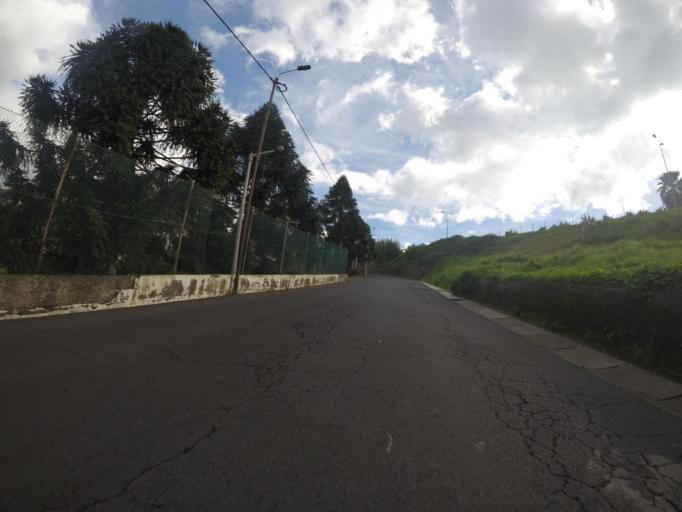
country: PT
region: Madeira
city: Camara de Lobos
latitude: 32.6484
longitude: -16.9546
